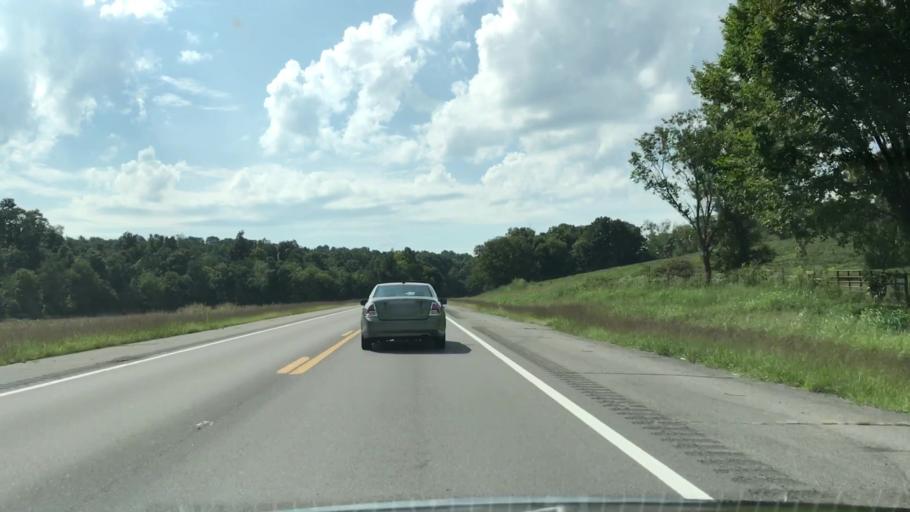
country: US
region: Tennessee
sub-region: Sumner County
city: Westmoreland
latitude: 36.6102
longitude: -86.2327
